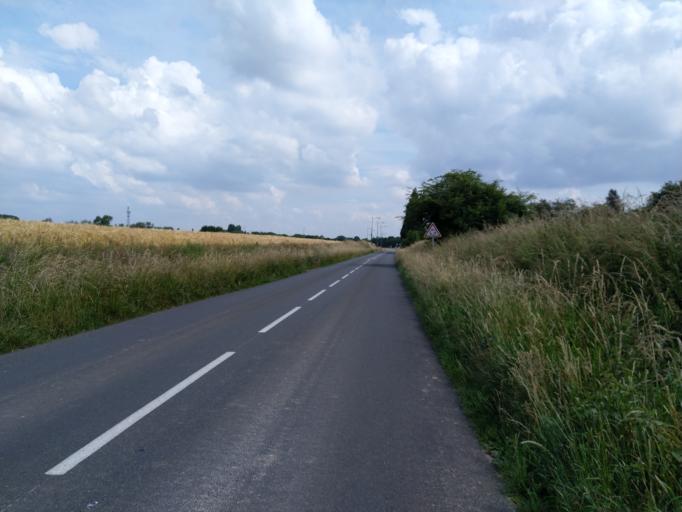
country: FR
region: Nord-Pas-de-Calais
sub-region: Departement du Nord
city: Rousies
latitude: 50.3097
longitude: 3.9988
